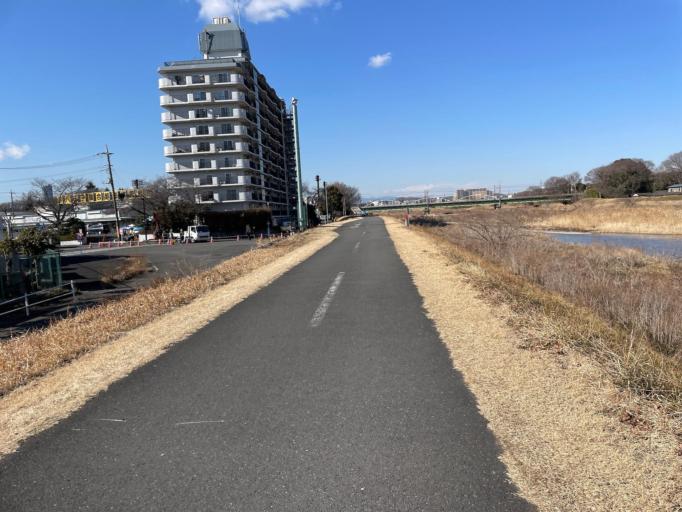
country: JP
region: Tokyo
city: Hachioji
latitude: 35.6485
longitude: 139.3623
